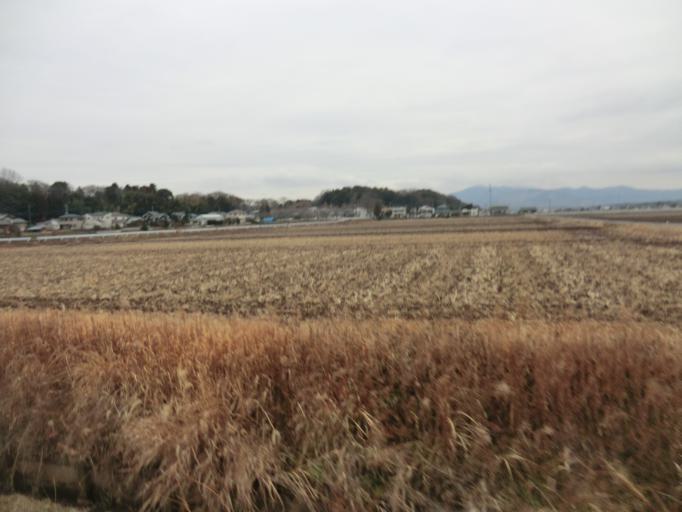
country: JP
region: Ibaraki
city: Naka
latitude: 36.0957
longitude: 140.1342
